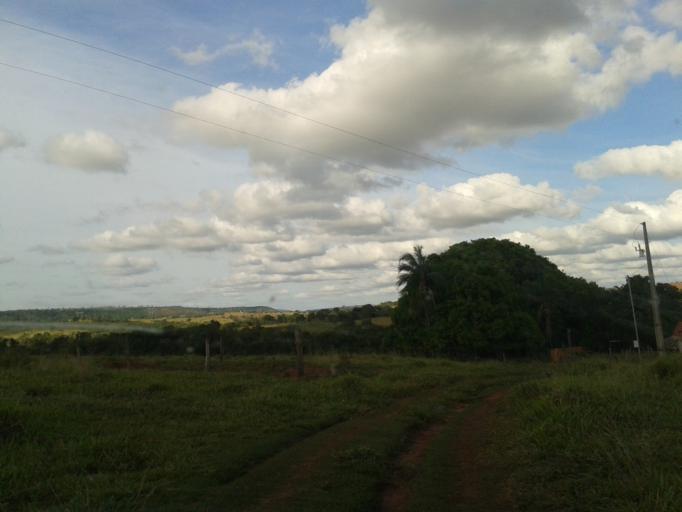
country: BR
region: Minas Gerais
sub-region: Campina Verde
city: Campina Verde
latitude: -19.4258
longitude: -49.7401
